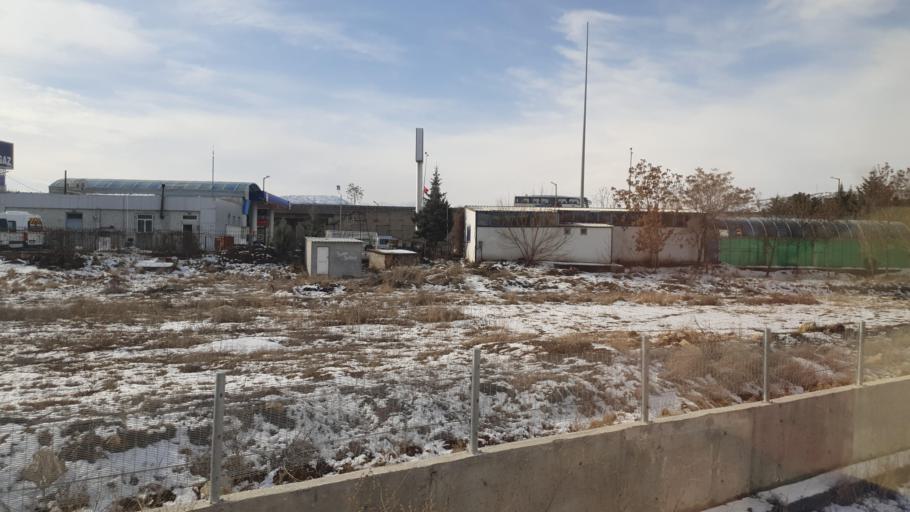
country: TR
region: Ankara
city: Elmadag
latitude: 39.9216
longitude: 33.2223
